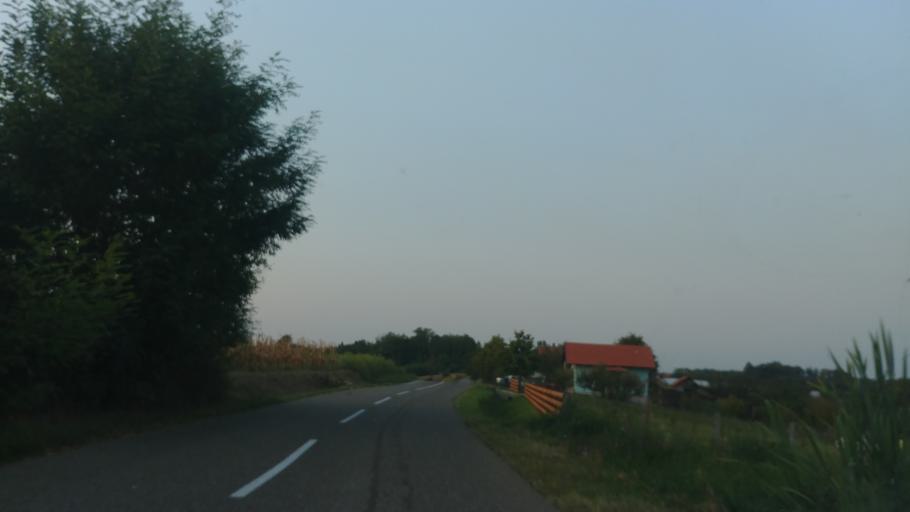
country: BA
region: Republika Srpska
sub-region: Opstina Ugljevik
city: Ugljevik
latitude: 44.7207
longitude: 18.9921
